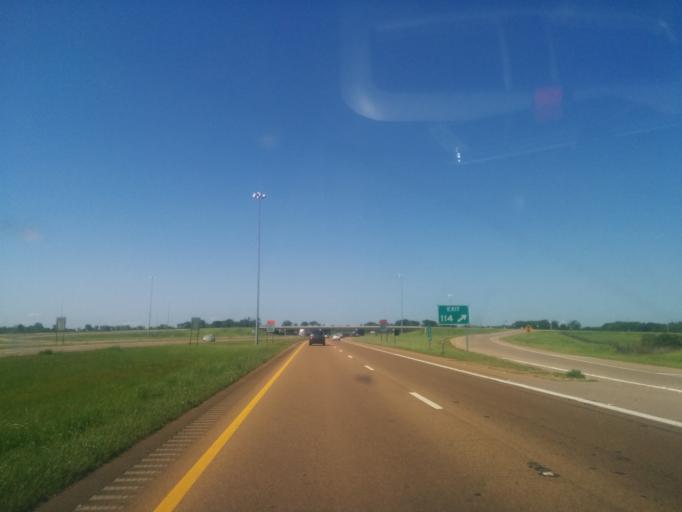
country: US
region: Mississippi
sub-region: Madison County
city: Madison
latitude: 32.5357
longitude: -90.0953
